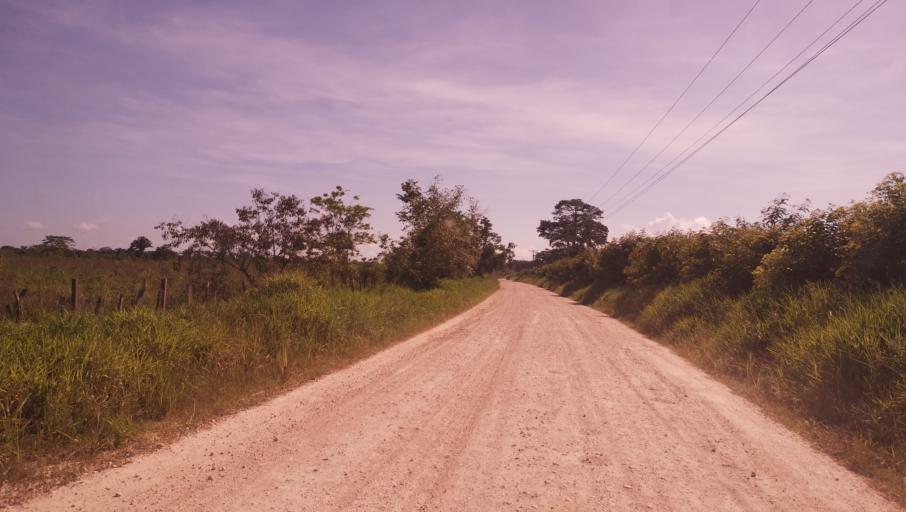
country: GT
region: Peten
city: Dolores
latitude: 16.7157
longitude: -89.3641
